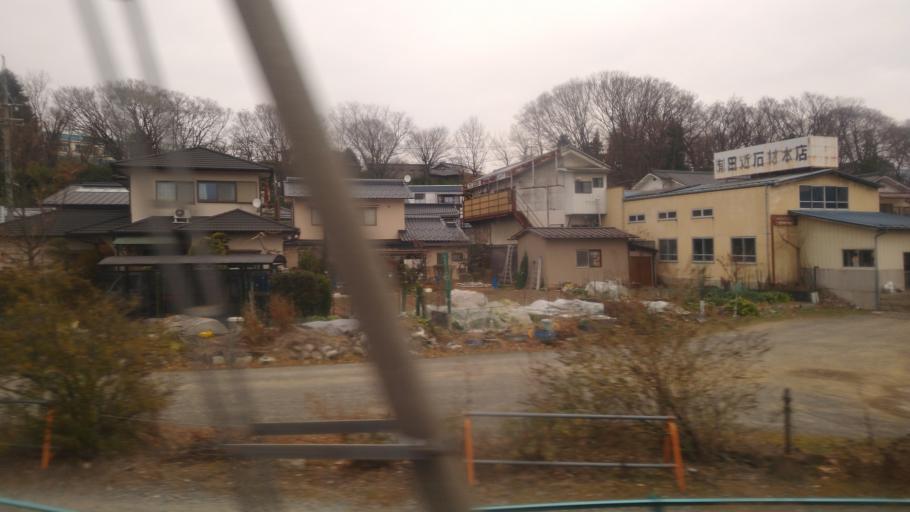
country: JP
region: Nagano
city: Matsumoto
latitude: 36.2408
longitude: 137.9562
